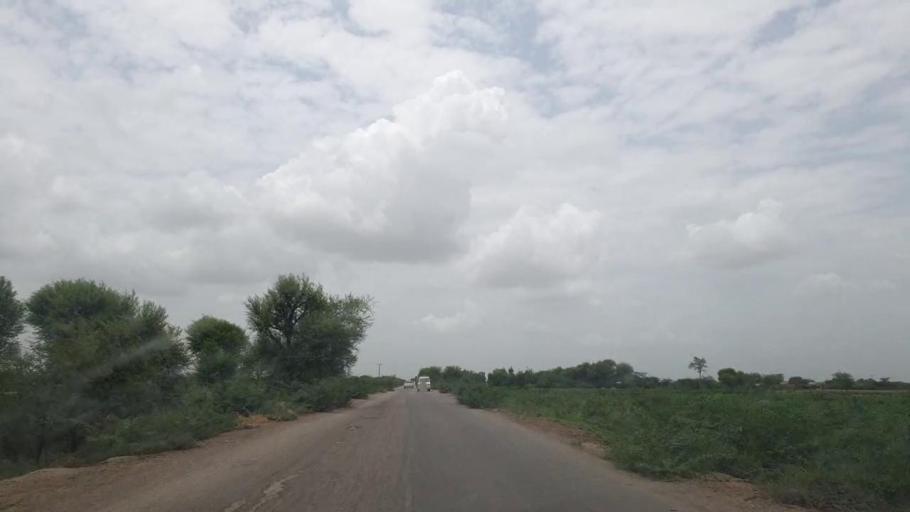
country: PK
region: Sindh
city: Naukot
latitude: 24.9299
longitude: 69.2761
